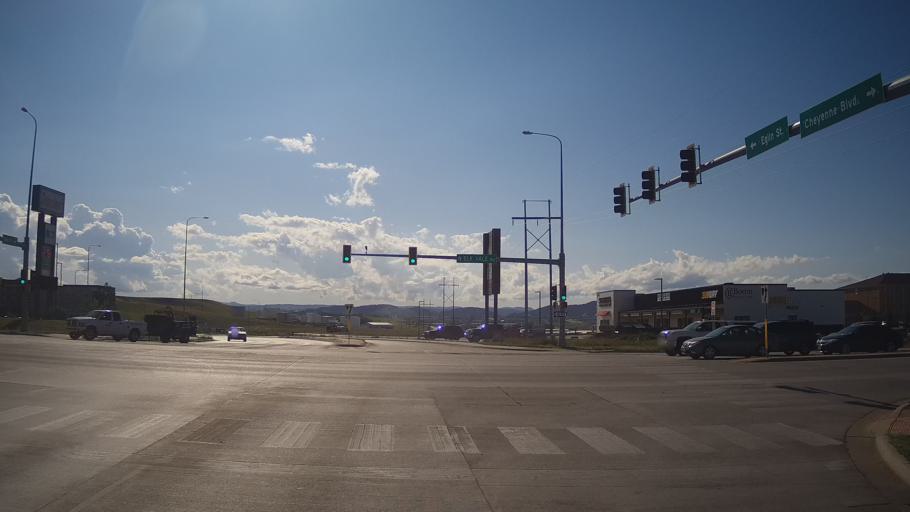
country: US
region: South Dakota
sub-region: Pennington County
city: Rapid Valley
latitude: 44.0964
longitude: -103.1508
